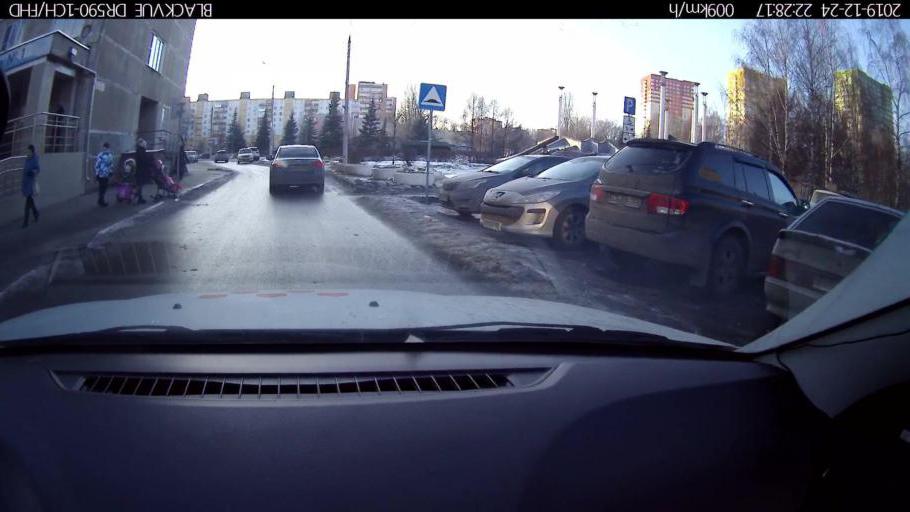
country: RU
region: Nizjnij Novgorod
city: Nizhniy Novgorod
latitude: 56.2383
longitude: 43.9623
